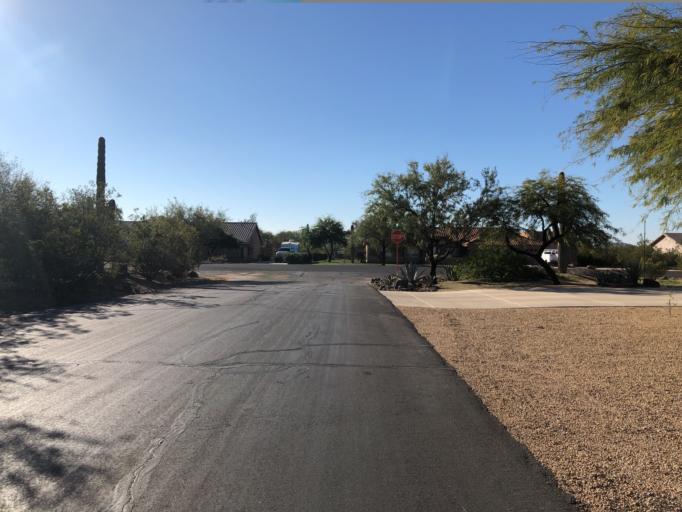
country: US
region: Arizona
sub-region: Maricopa County
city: Anthem
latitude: 33.8359
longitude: -112.0703
